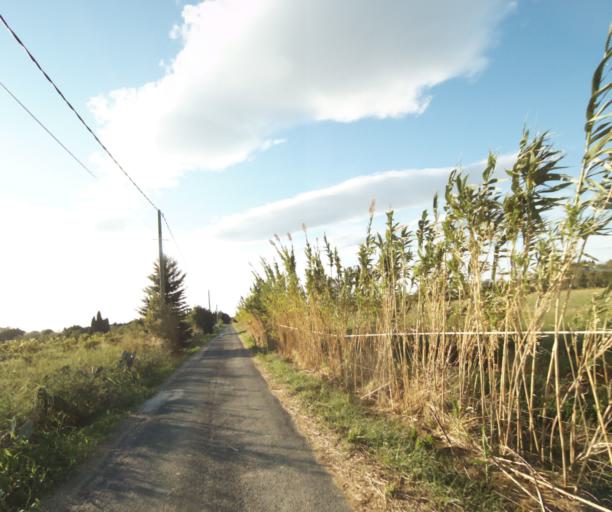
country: FR
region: Languedoc-Roussillon
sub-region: Departement des Pyrenees-Orientales
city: Latour-Bas-Elne
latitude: 42.5802
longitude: 3.0004
